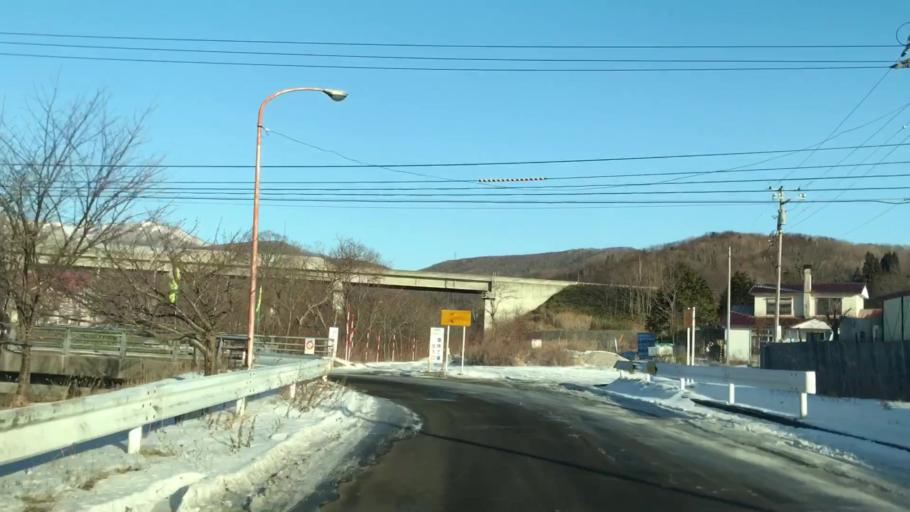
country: JP
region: Hokkaido
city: Muroran
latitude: 42.3891
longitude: 141.0687
